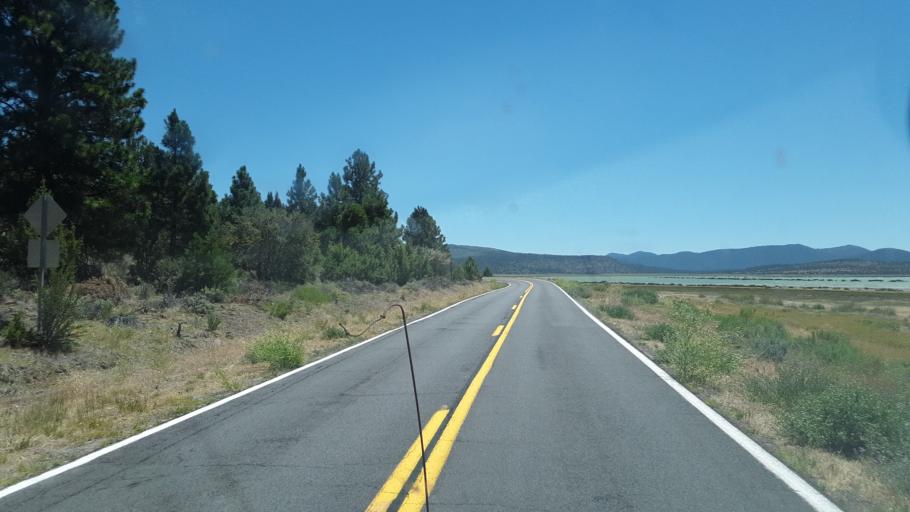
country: US
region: California
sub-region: Lassen County
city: Susanville
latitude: 40.6865
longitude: -120.6628
